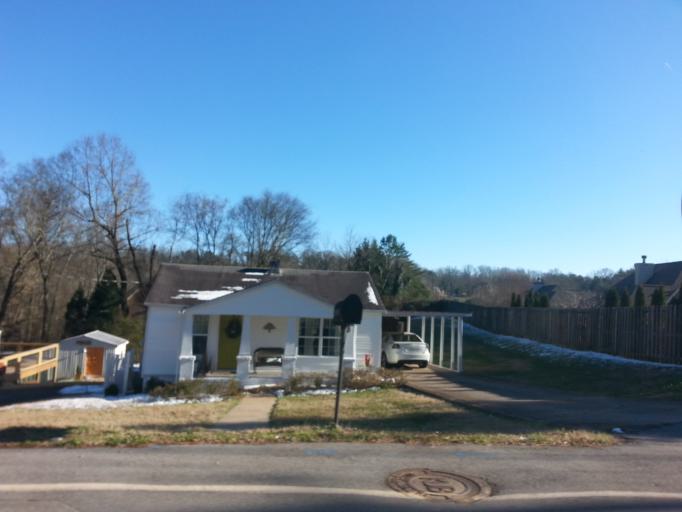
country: US
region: Tennessee
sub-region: Knox County
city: Knoxville
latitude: 35.9077
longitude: -83.9984
